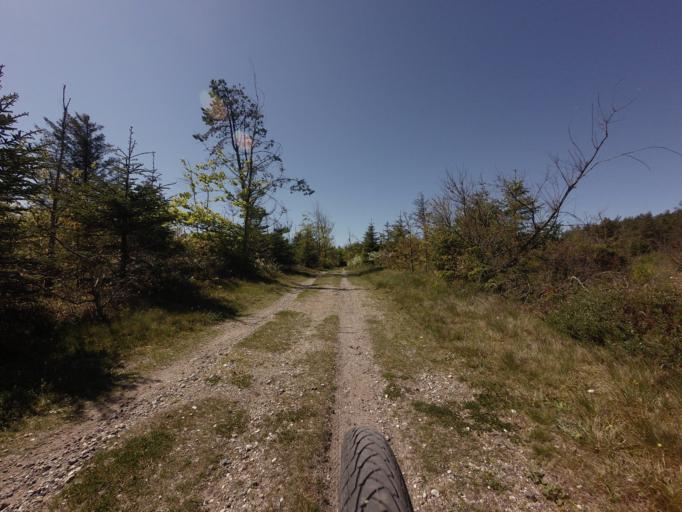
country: DK
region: North Denmark
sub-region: Jammerbugt Kommune
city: Pandrup
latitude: 57.2712
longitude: 9.6280
